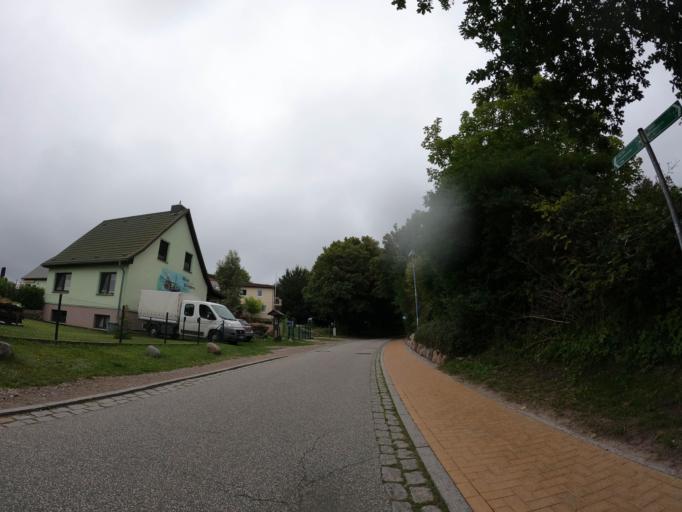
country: DE
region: Mecklenburg-Vorpommern
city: Ostseebad Gohren
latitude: 54.3367
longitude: 13.7399
